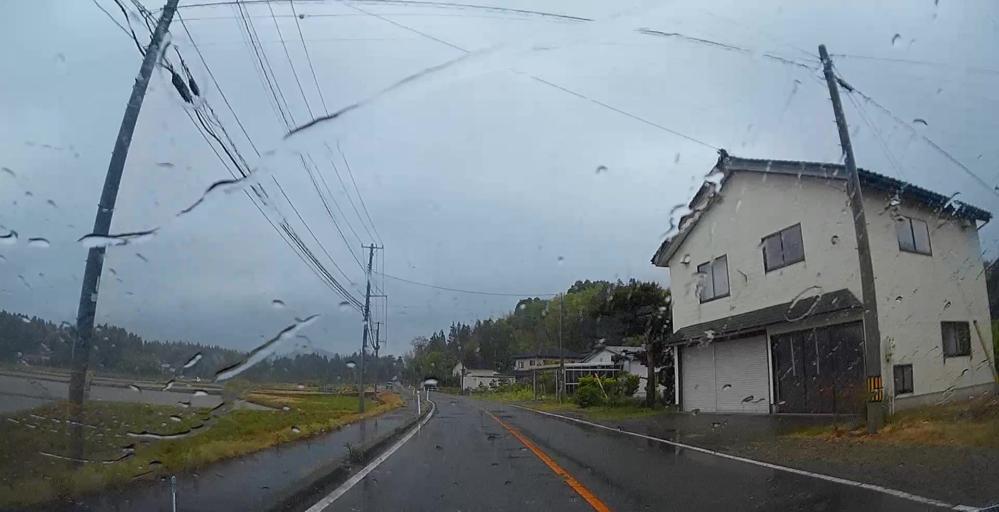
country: JP
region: Niigata
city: Kashiwazaki
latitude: 37.4464
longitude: 138.6434
